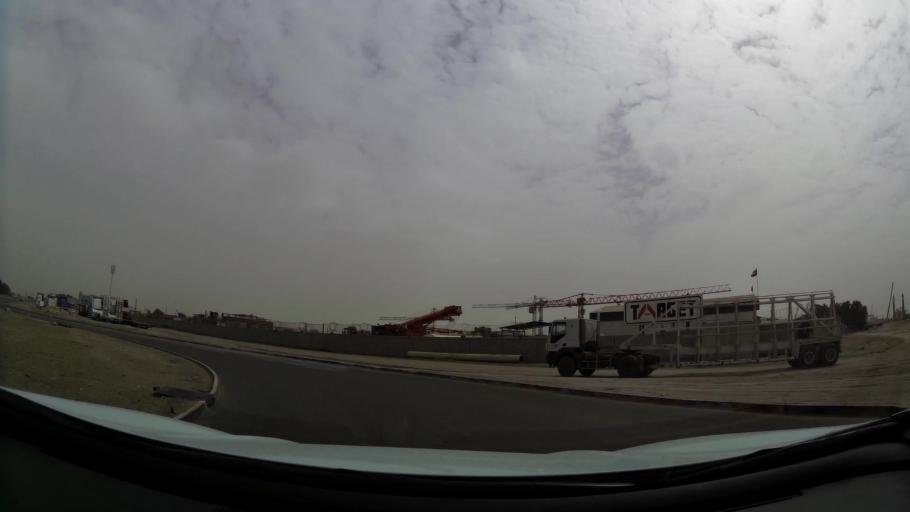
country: AE
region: Abu Dhabi
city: Abu Dhabi
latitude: 24.3531
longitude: 54.4599
